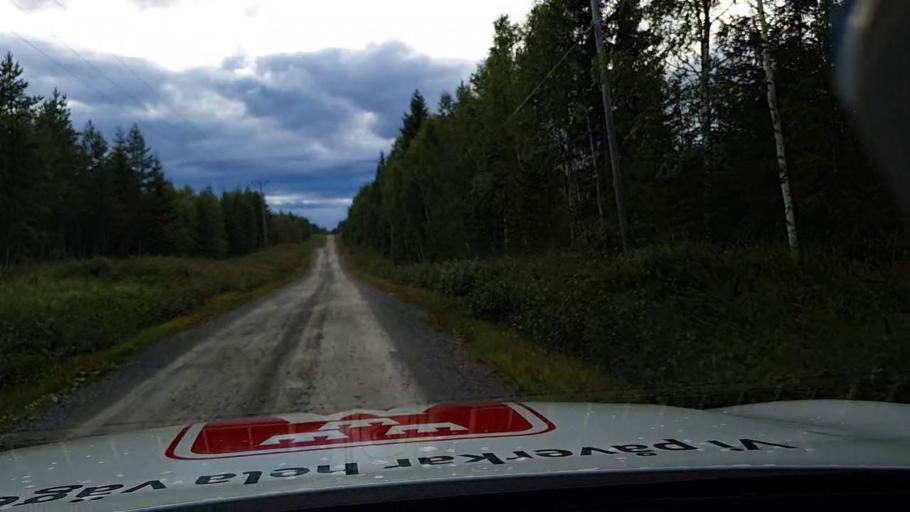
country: SE
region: Jaemtland
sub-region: Bergs Kommun
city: Hoverberg
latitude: 62.8869
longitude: 14.5776
